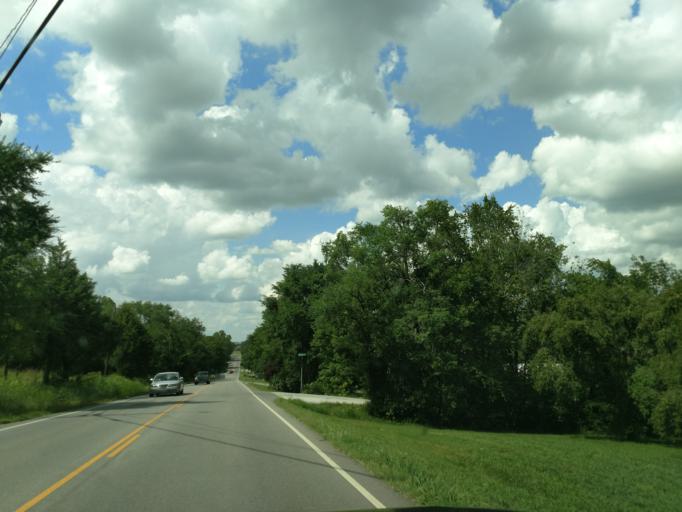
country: US
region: Arkansas
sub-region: Carroll County
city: Berryville
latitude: 36.3788
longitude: -93.5673
